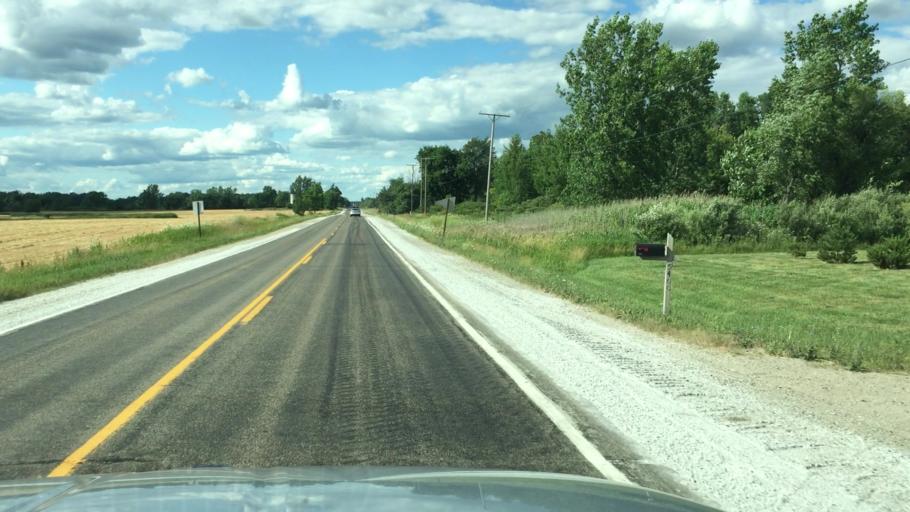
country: US
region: Michigan
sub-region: Saint Clair County
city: Capac
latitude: 43.0531
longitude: -82.9296
